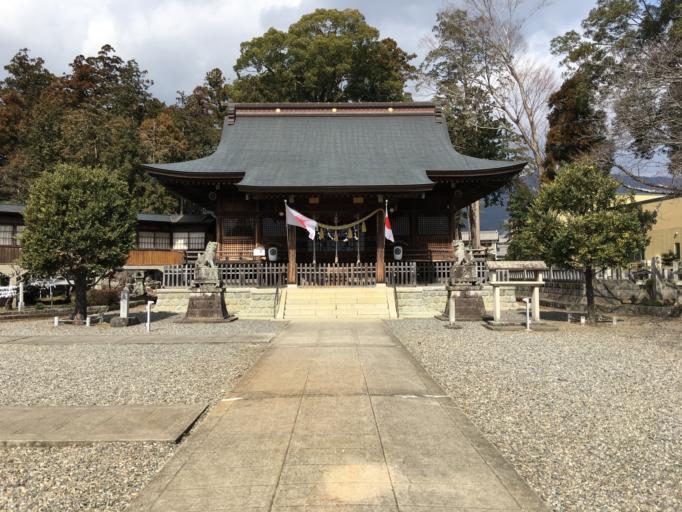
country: JP
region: Aichi
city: Shinshiro
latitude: 34.9029
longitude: 137.4937
